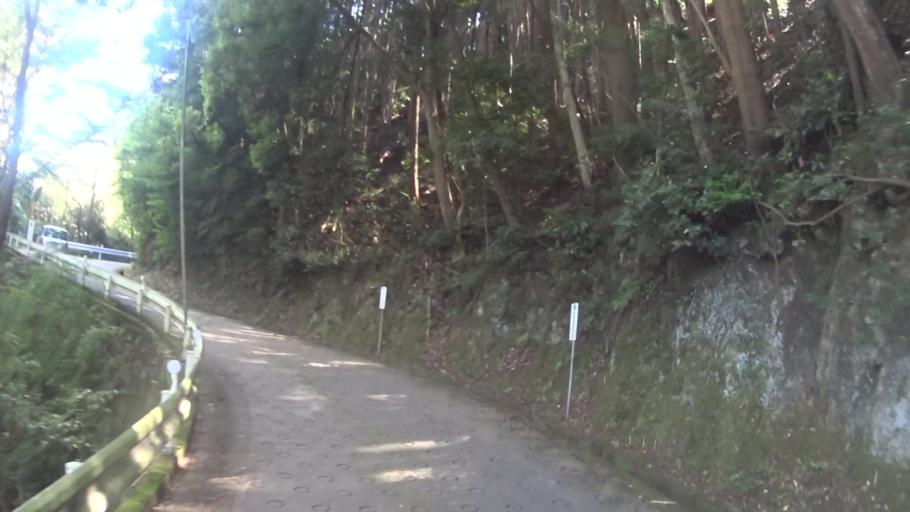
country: JP
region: Nara
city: Nara-shi
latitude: 34.7573
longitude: 135.9393
